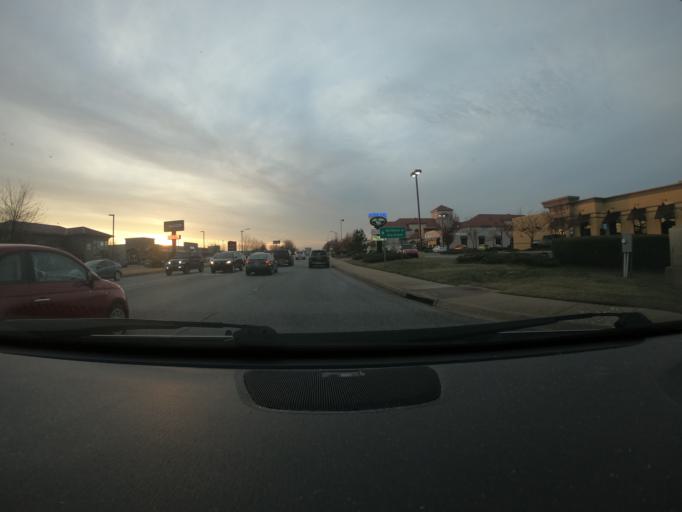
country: US
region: Arkansas
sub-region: Benton County
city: Bentonville
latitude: 36.3354
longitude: -94.1976
